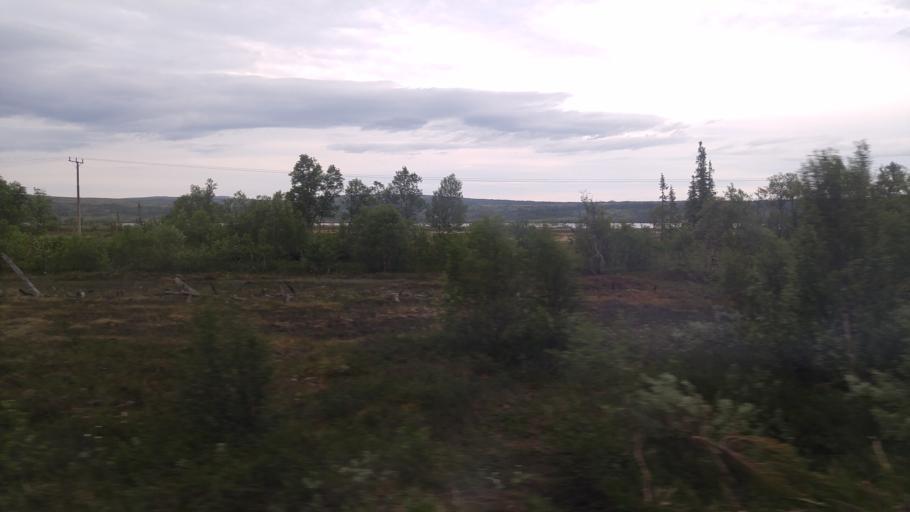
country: NO
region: Nord-Trondelag
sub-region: Meraker
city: Meraker
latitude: 63.3156
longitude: 12.2217
